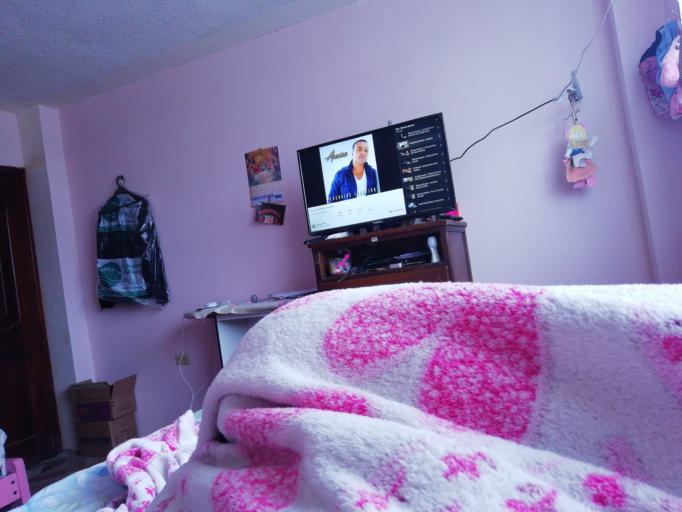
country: EC
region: Chimborazo
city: Riobamba
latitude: -1.7278
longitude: -78.6007
